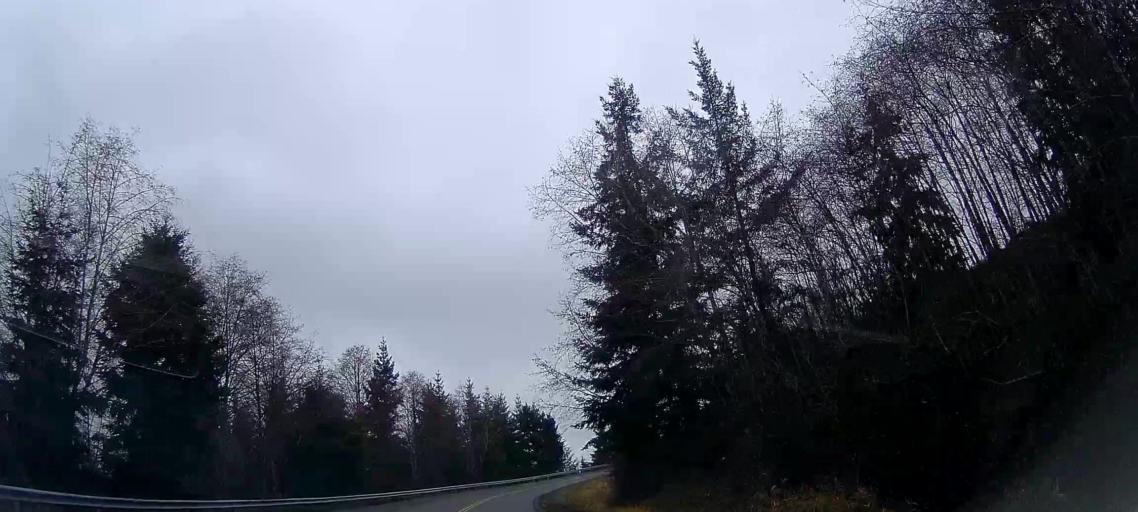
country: US
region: Washington
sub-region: Skagit County
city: Mount Vernon
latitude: 48.3775
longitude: -122.2991
